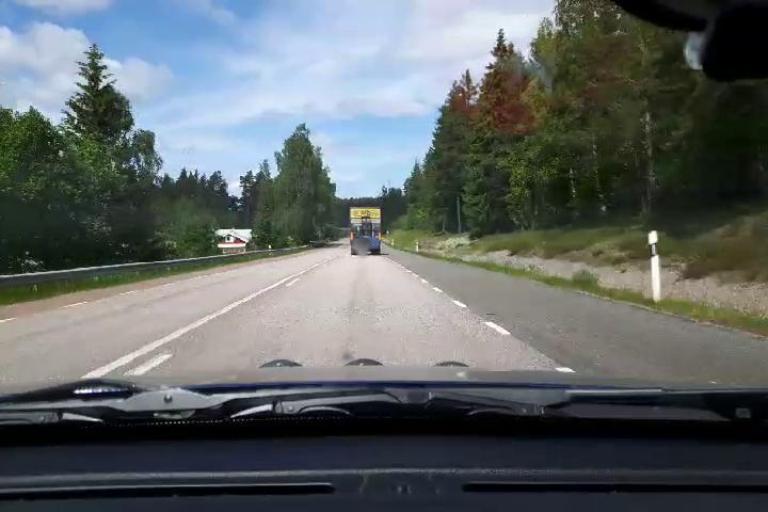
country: SE
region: Uppsala
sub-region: Osthammars Kommun
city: Bjorklinge
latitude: 60.0952
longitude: 17.5541
